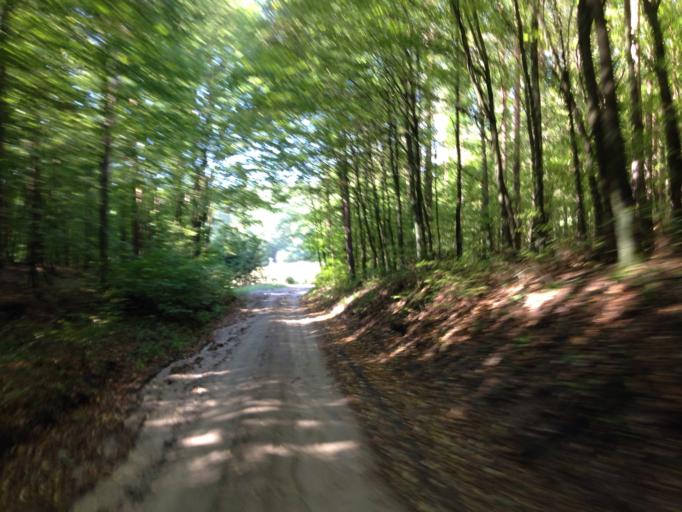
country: PL
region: Kujawsko-Pomorskie
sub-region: Powiat brodnicki
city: Gorzno
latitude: 53.2257
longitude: 19.7200
